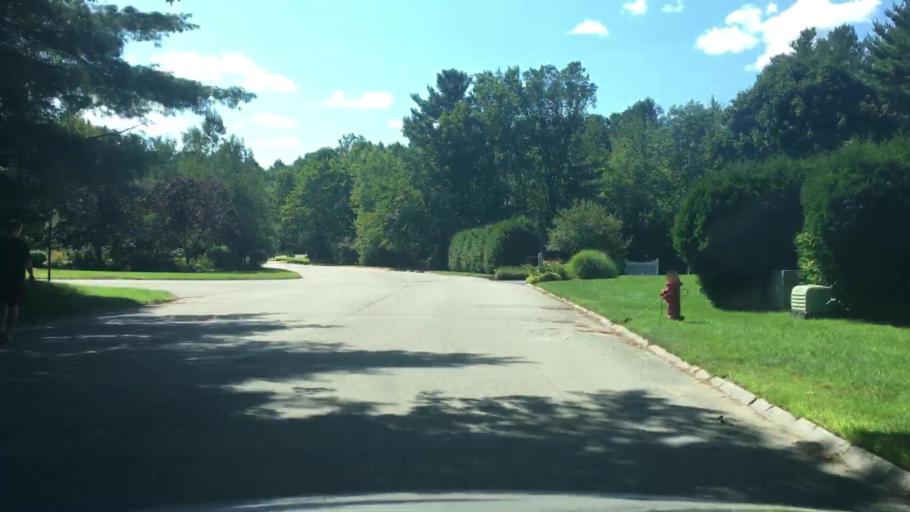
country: US
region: Maine
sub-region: York County
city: Eliot
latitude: 43.1713
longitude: -70.8376
